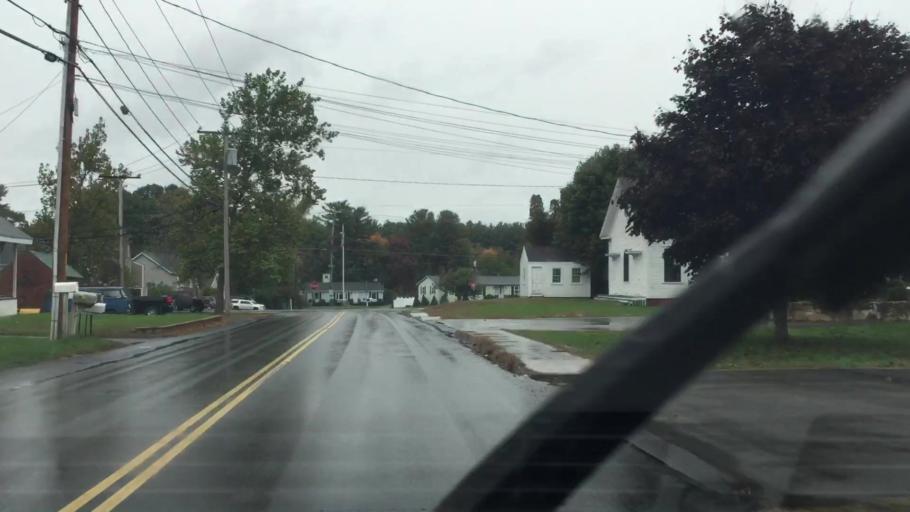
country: US
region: New Hampshire
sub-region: Rockingham County
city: Seabrook
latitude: 42.8750
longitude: -70.8568
